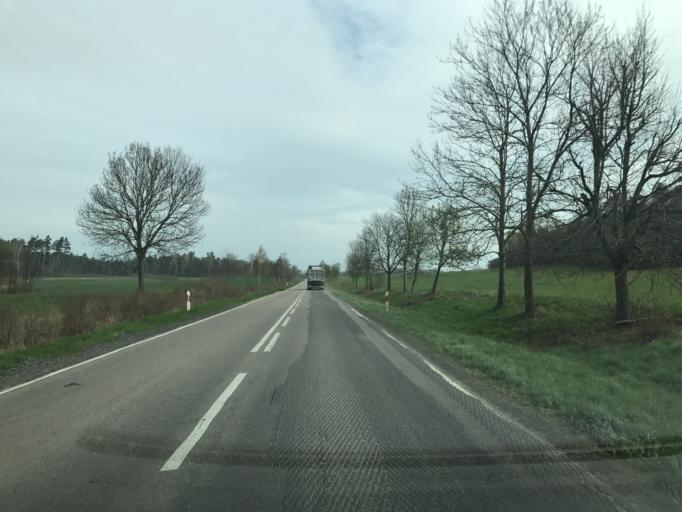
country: PL
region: Warmian-Masurian Voivodeship
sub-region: Powiat ostrodzki
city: Gierzwald
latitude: 53.5528
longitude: 20.0910
